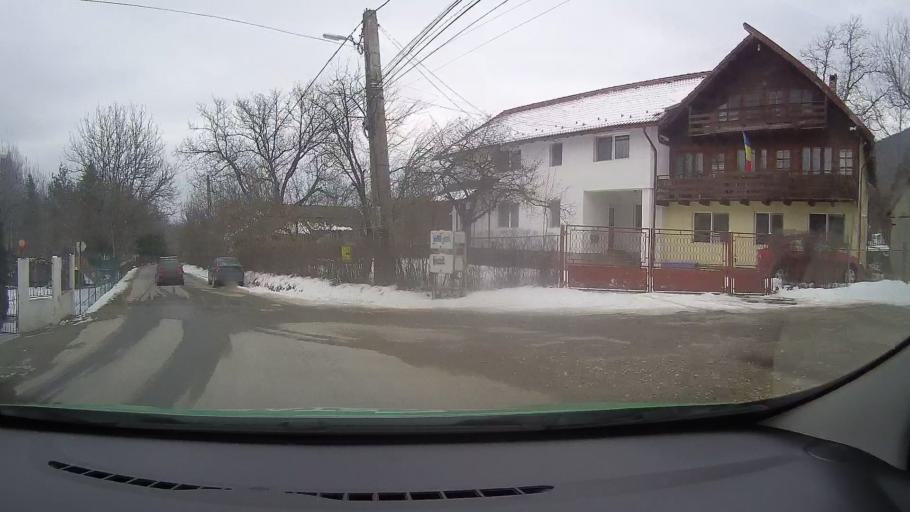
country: RO
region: Brasov
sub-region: Comuna Bran
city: Bran
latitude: 45.5306
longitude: 25.3502
